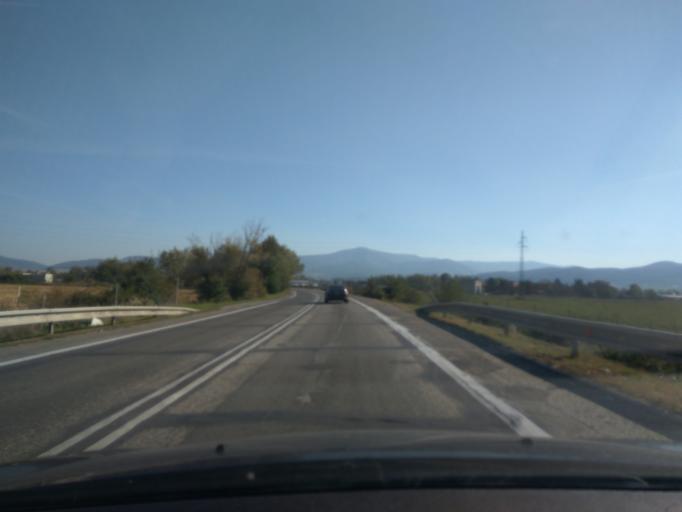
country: SK
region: Trenciansky
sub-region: Okres Trencin
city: Trencin
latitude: 48.8573
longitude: 17.9597
